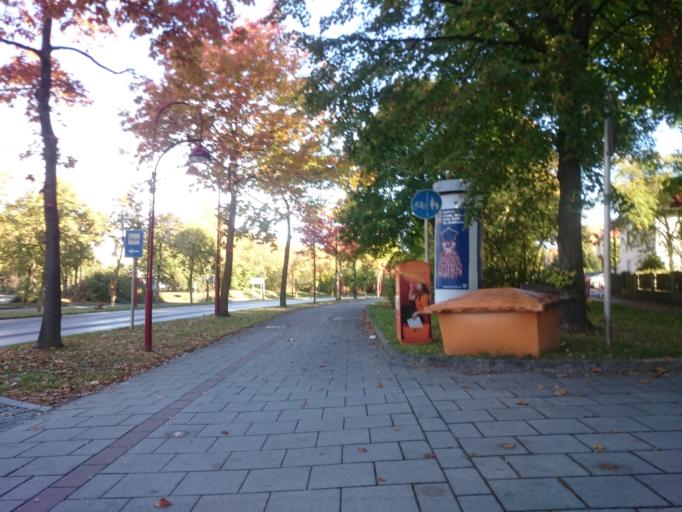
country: DE
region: Bavaria
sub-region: Swabia
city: Gersthofen
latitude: 48.4124
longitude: 10.8793
